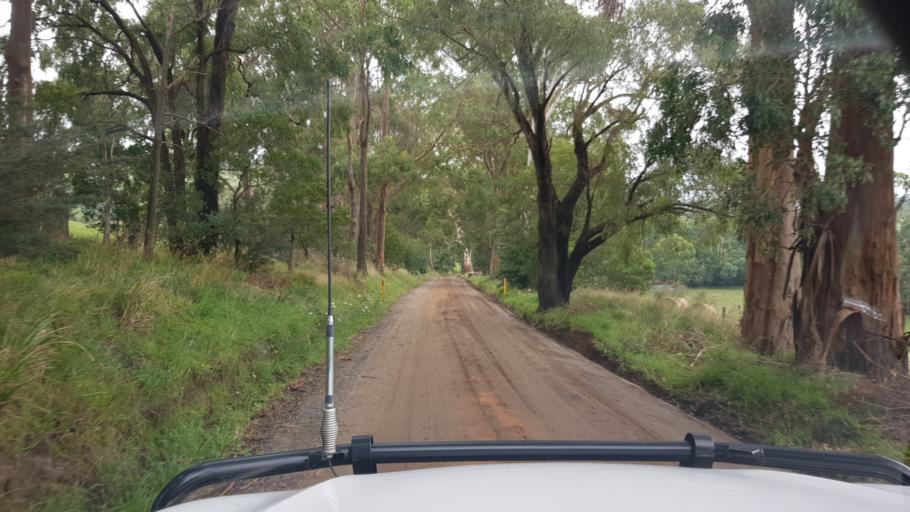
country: AU
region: Victoria
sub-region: Latrobe
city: Moe
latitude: -38.0745
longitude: 146.1465
